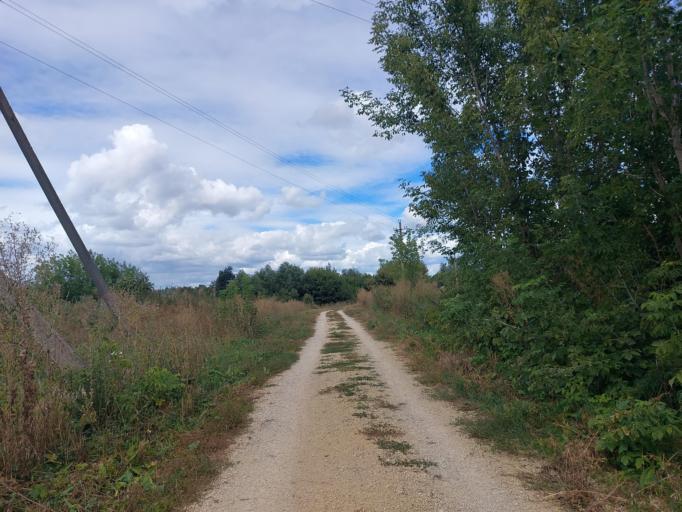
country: RU
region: Lipetsk
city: Terbuny
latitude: 52.2606
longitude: 38.2073
